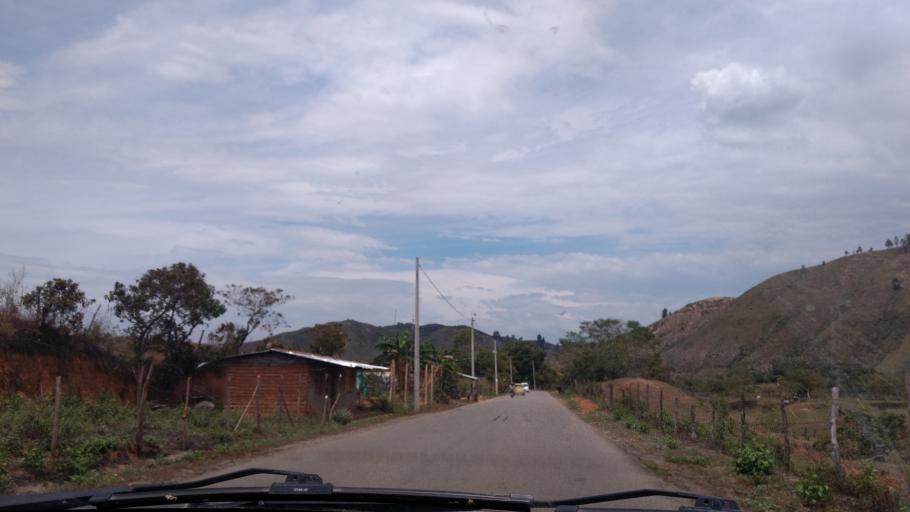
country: CO
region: Cauca
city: Buenos Aires
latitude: 3.0483
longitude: -76.6586
